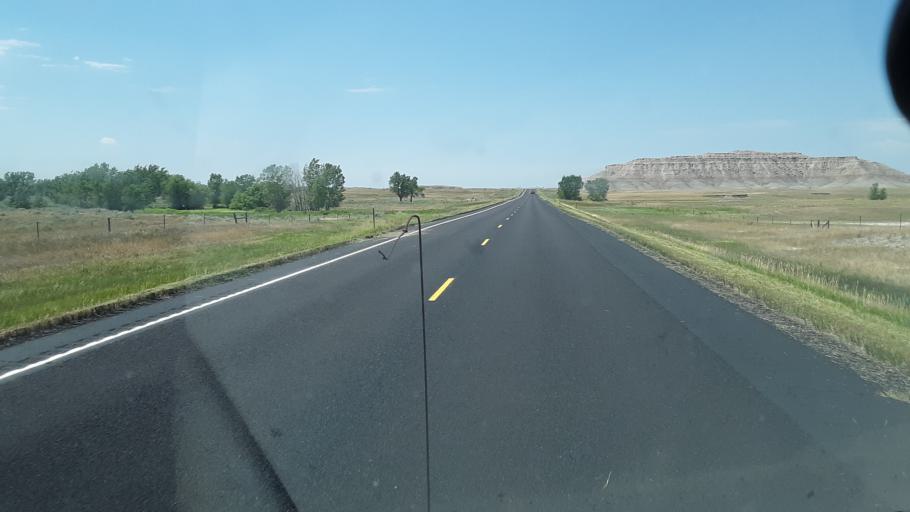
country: US
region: South Dakota
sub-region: Haakon County
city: Philip
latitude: 43.7193
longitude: -102.0101
